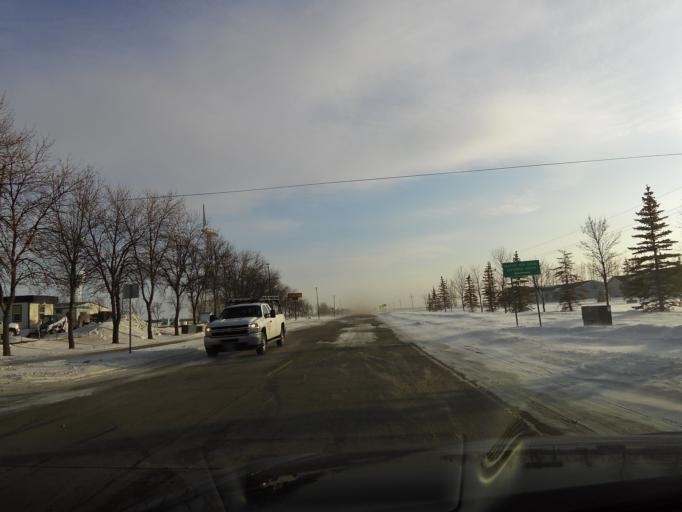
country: US
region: North Dakota
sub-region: Walsh County
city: Grafton
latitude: 48.4073
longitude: -97.4267
